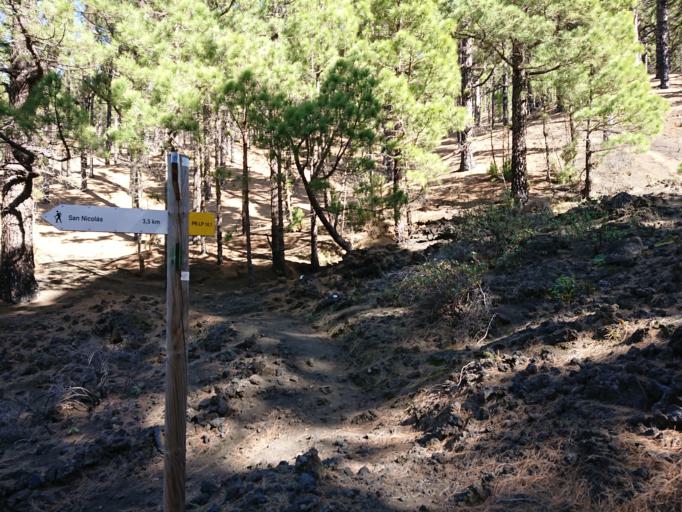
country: ES
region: Canary Islands
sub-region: Provincia de Santa Cruz de Tenerife
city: El Paso
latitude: 28.6036
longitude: -17.8586
